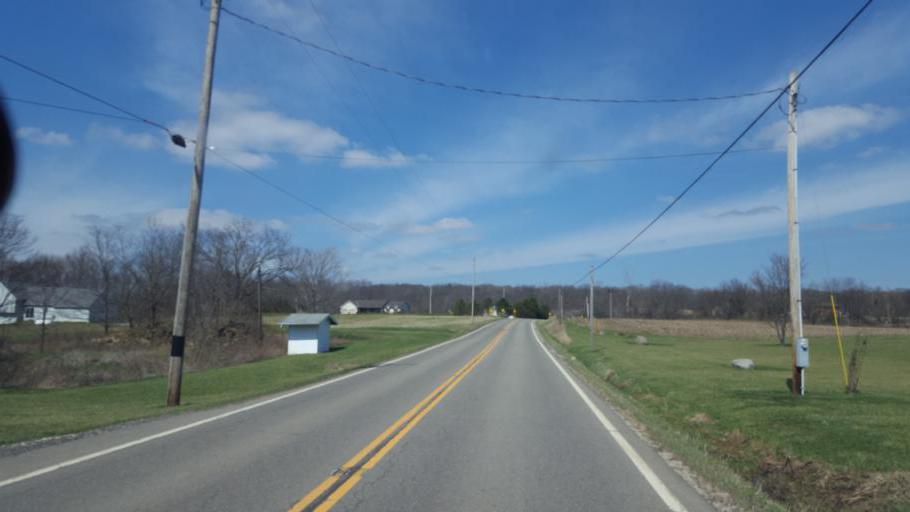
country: US
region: Ohio
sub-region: Richland County
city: Lincoln Heights
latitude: 40.8715
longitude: -82.4411
